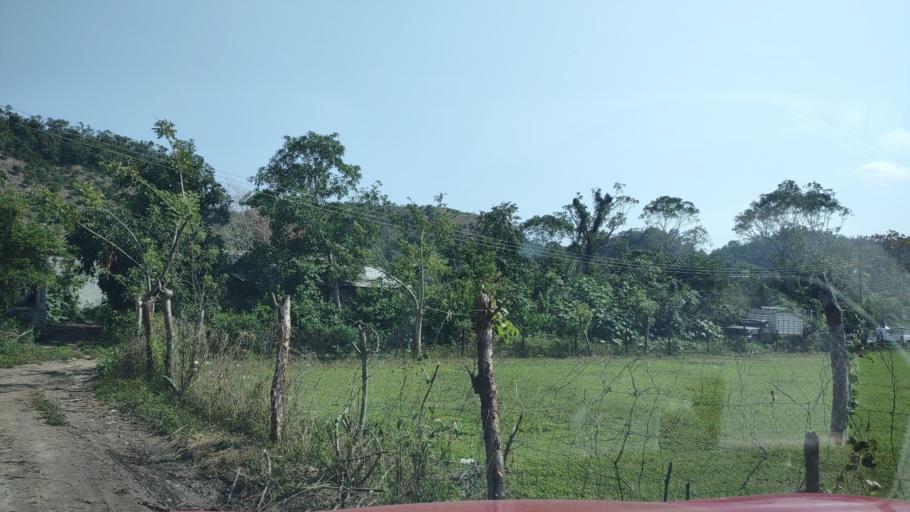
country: MX
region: Veracruz
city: Agua Dulce
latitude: 20.3109
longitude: -97.1746
